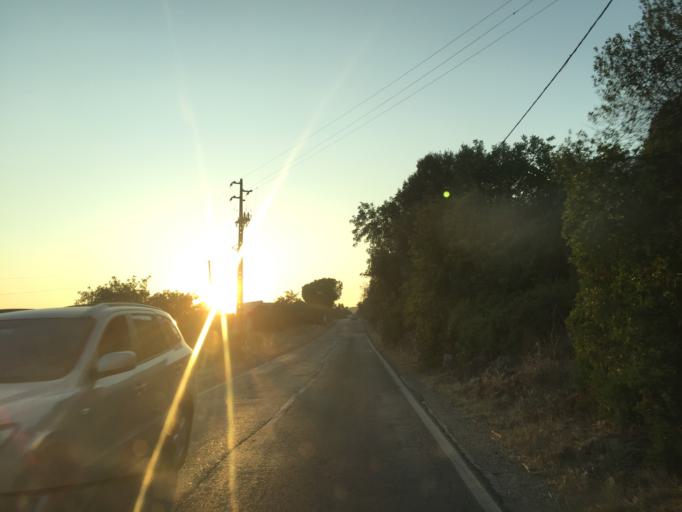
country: PT
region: Faro
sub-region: Faro
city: Santa Barbara de Nexe
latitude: 37.0977
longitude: -7.9553
